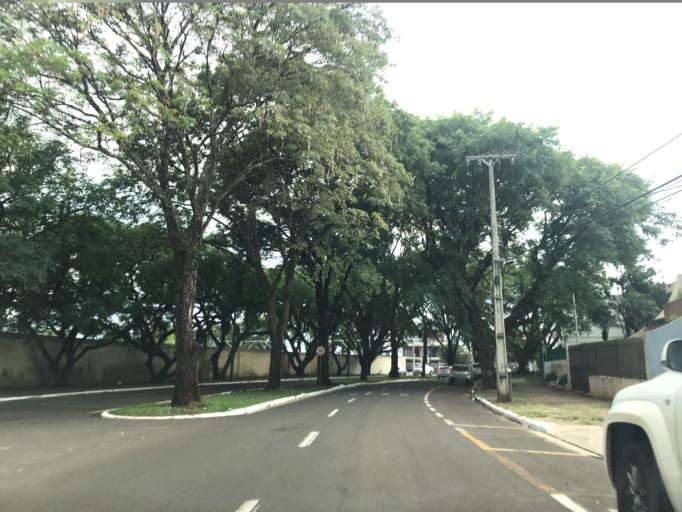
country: BR
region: Parana
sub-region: Maringa
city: Maringa
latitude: -23.4351
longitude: -51.9477
